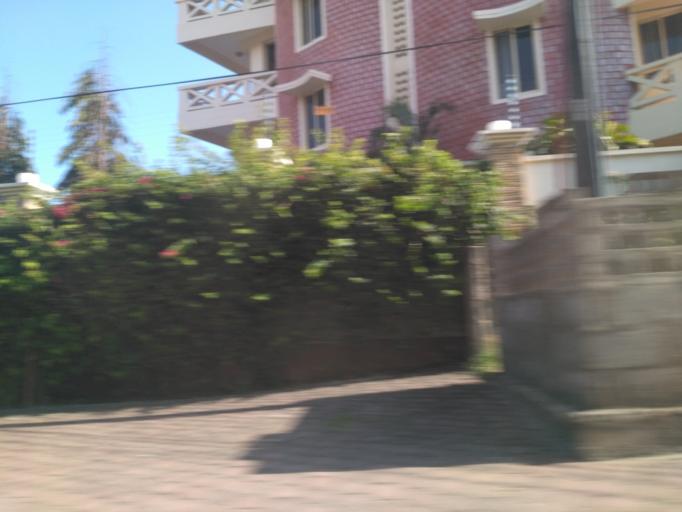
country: TZ
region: Dar es Salaam
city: Magomeni
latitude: -6.7496
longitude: 39.2870
